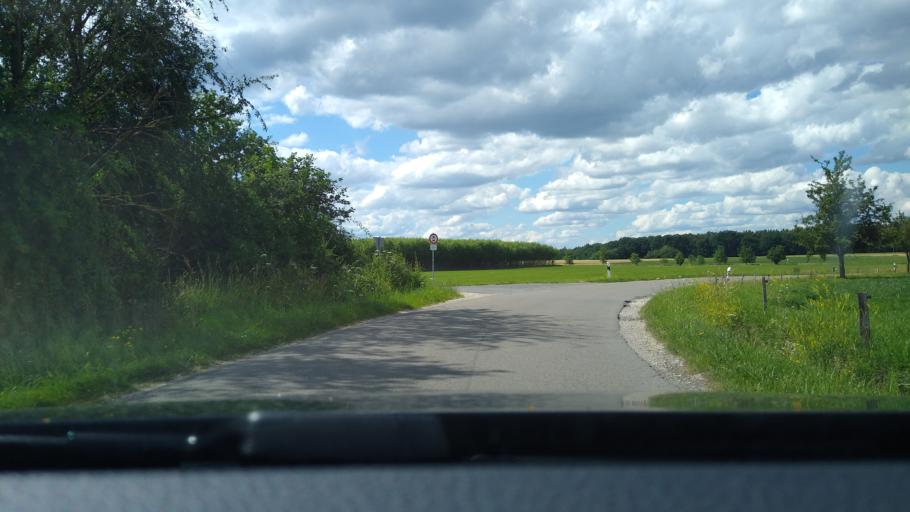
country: DE
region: Bavaria
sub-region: Regierungsbezirk Mittelfranken
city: Absberg
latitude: 49.1678
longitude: 10.8852
